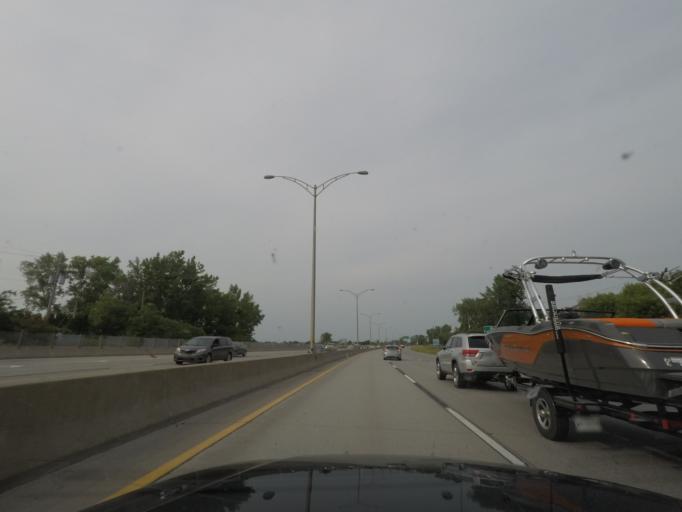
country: CA
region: Quebec
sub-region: Monteregie
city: La Prairie
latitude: 45.4220
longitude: -73.4967
